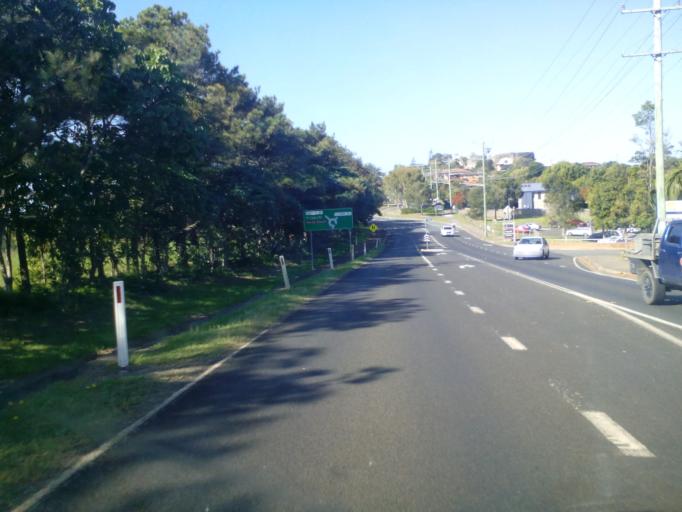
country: AU
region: New South Wales
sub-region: Tweed
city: Kingscliff
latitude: -28.2638
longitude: 153.5687
